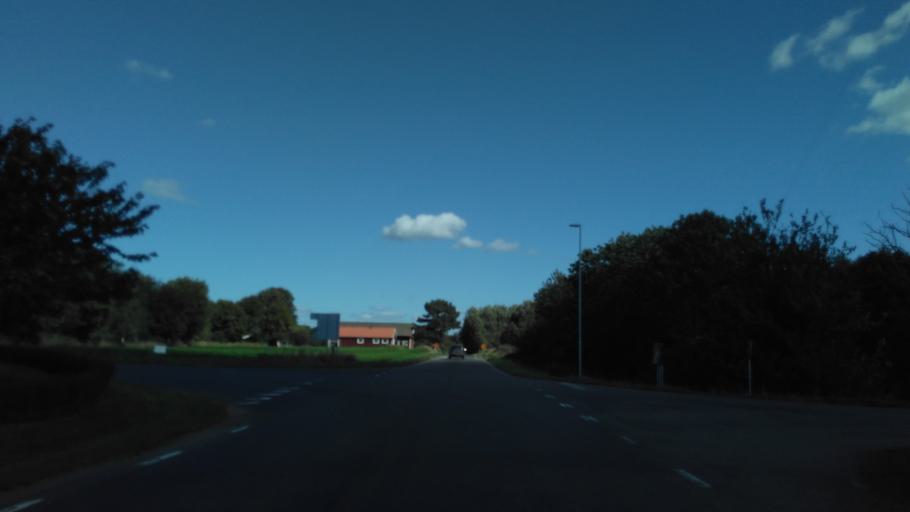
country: SE
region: Vaestra Goetaland
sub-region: Skara Kommun
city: Axvall
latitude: 58.4338
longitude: 13.6438
